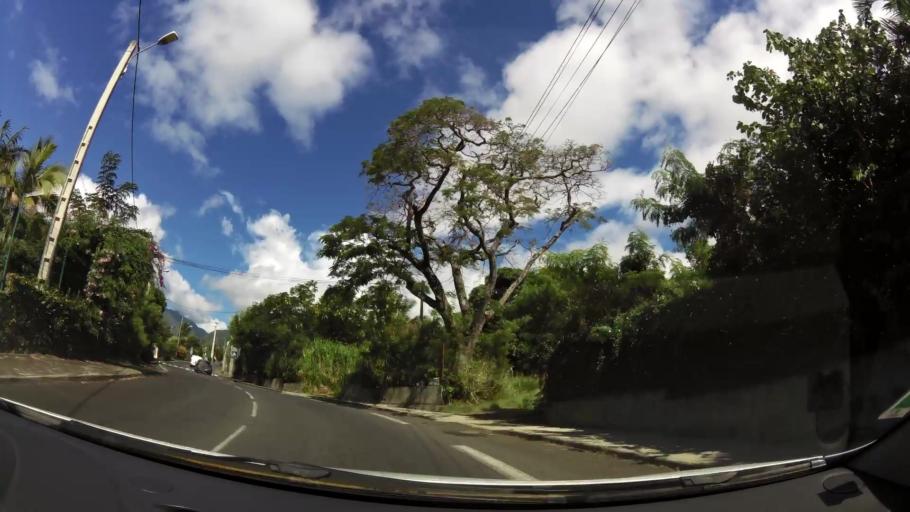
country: RE
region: Reunion
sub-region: Reunion
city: Sainte-Marie
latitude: -20.9118
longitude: 55.4981
